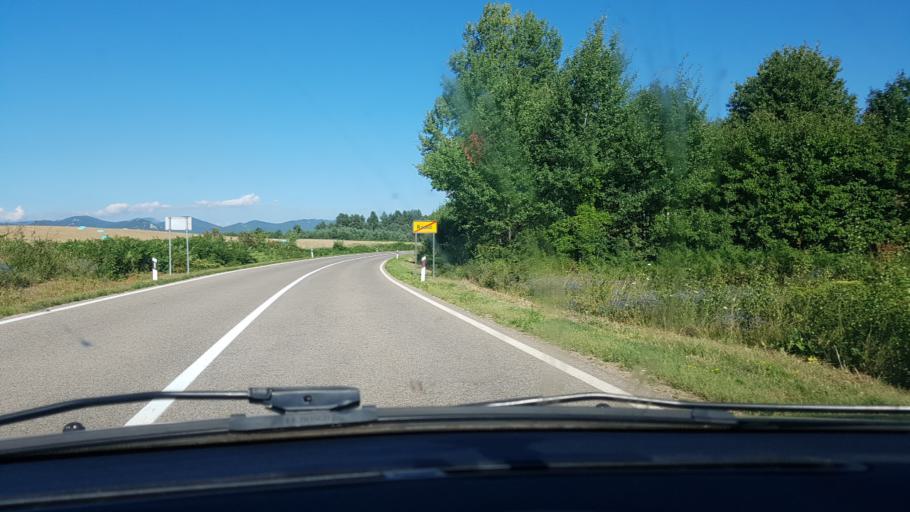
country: HR
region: Zadarska
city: Starigrad
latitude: 44.3889
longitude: 15.6152
